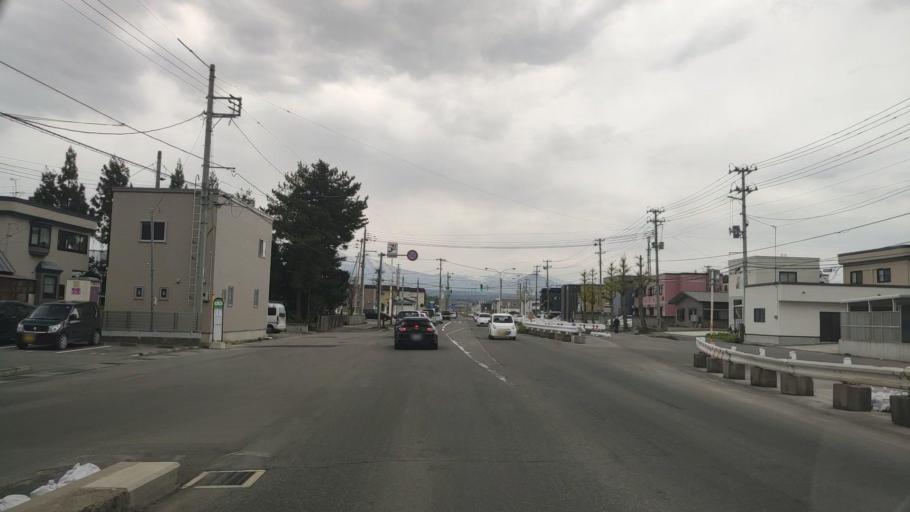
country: JP
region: Aomori
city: Aomori Shi
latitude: 40.8060
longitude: 140.7806
